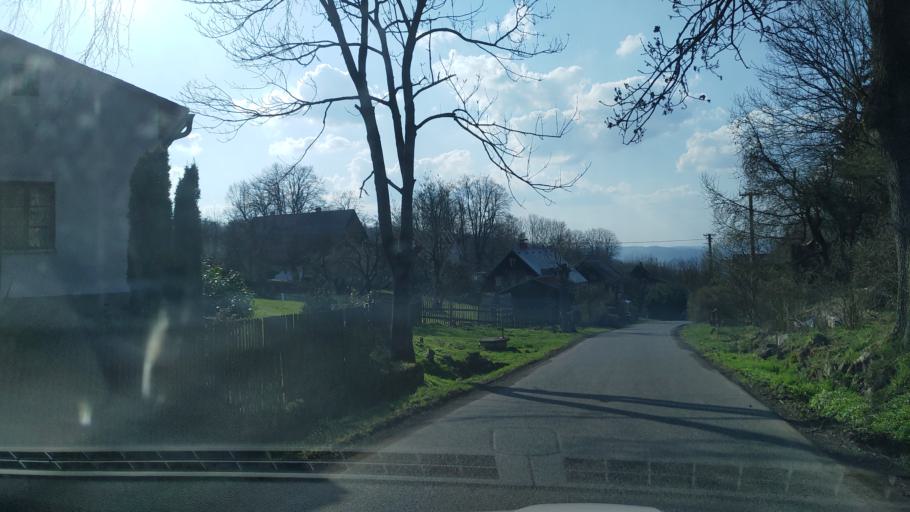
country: CZ
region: Ustecky
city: Vernerice
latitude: 50.6902
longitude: 14.2574
